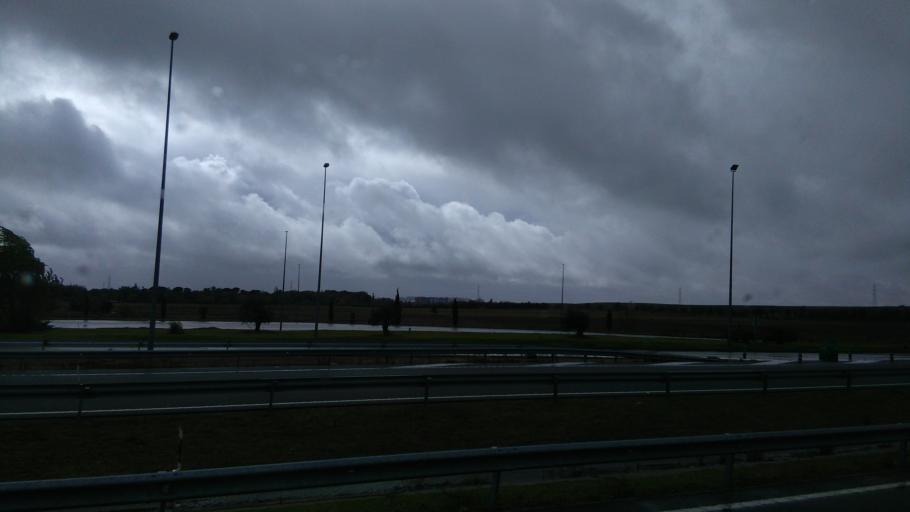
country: ES
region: Madrid
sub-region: Provincia de Madrid
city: Alcorcon
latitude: 40.3364
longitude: -3.8050
